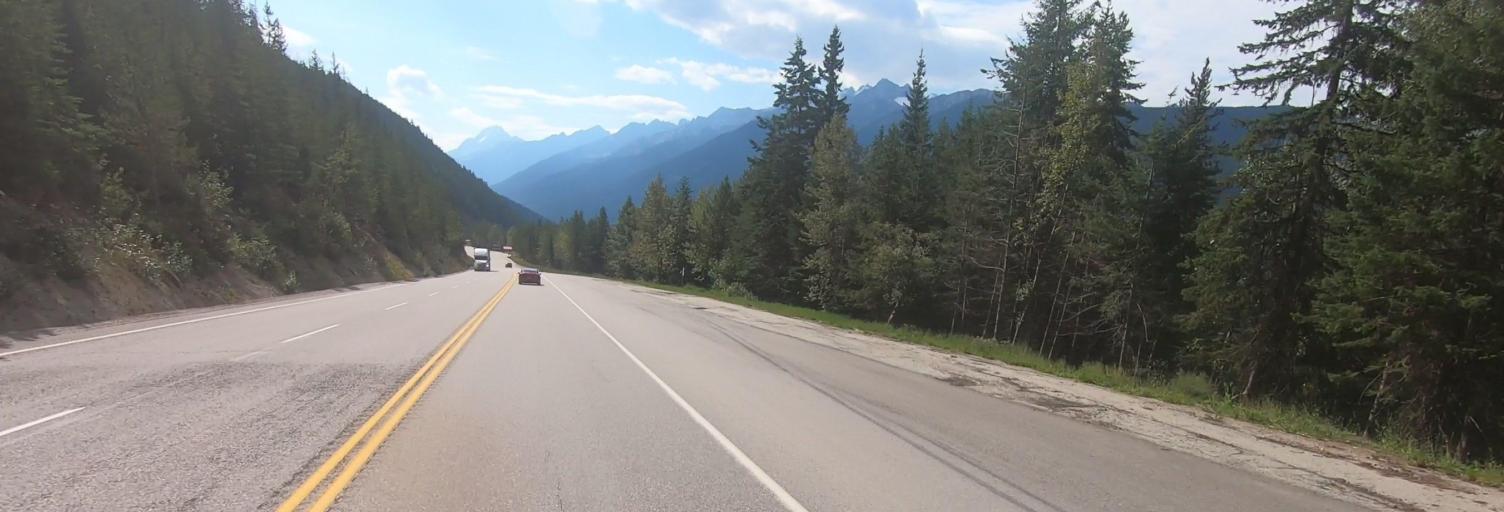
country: CA
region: British Columbia
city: Golden
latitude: 51.4674
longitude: -117.4812
